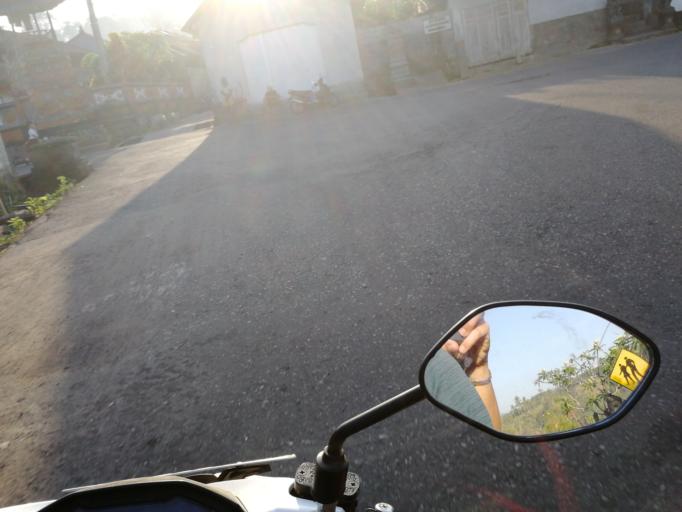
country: ID
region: Bali
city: Tistagede
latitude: -8.3875
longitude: 115.6160
